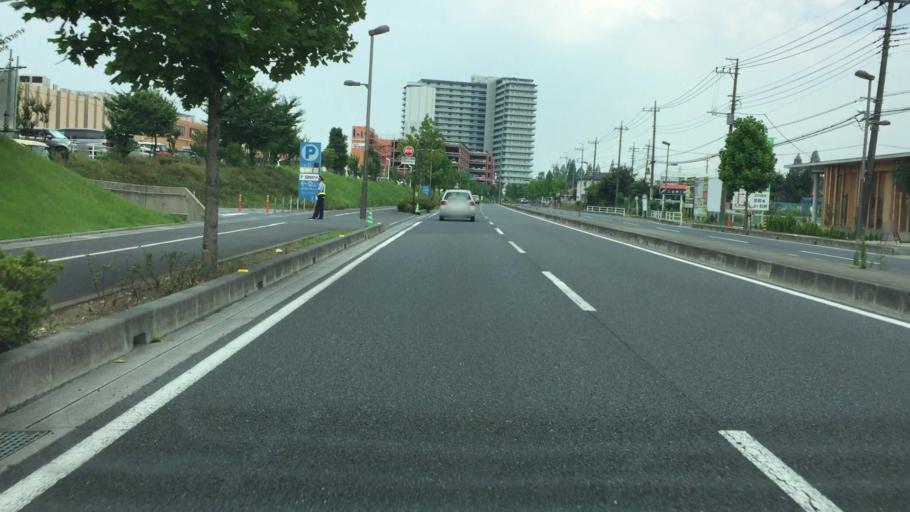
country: JP
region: Saitama
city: Yoshikawa
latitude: 35.8601
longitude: 139.8637
